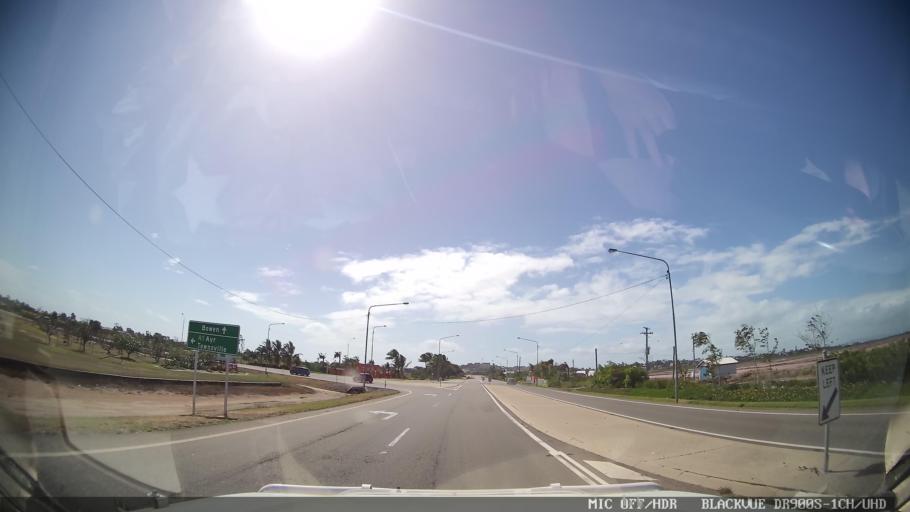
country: AU
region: Queensland
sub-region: Whitsunday
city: Bowen
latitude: -20.0156
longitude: 148.2208
